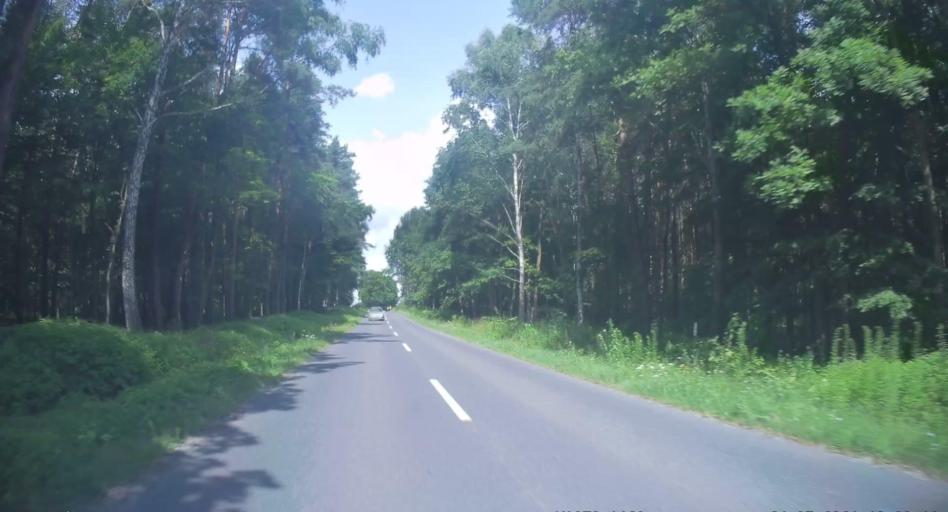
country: PL
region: Lodz Voivodeship
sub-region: Powiat tomaszowski
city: Lubochnia
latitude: 51.5600
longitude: 20.1278
